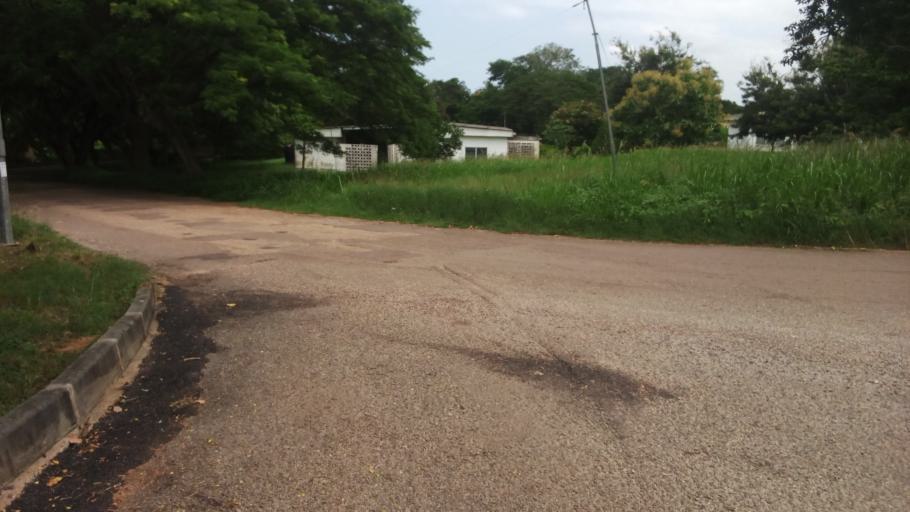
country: GH
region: Central
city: Cape Coast
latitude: 5.1281
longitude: -1.2850
